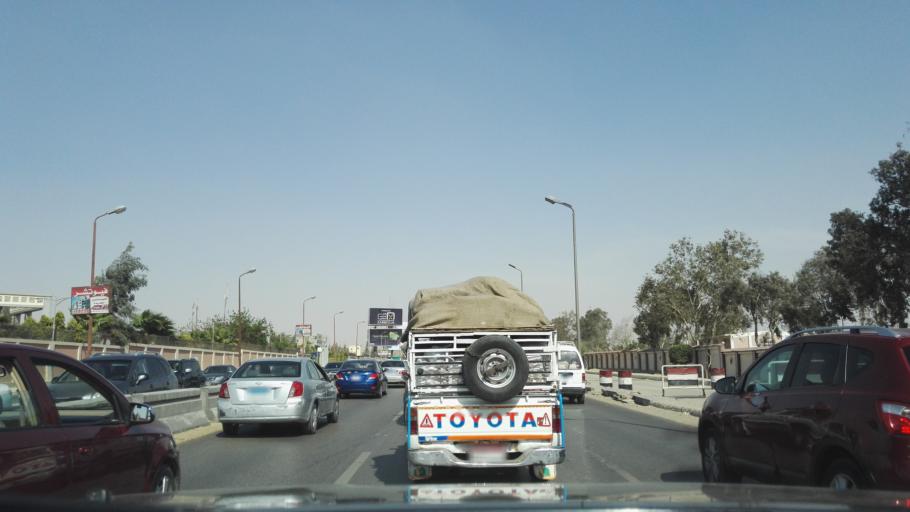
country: EG
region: Muhafazat al Qalyubiyah
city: Al Khankah
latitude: 30.0811
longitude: 31.4052
